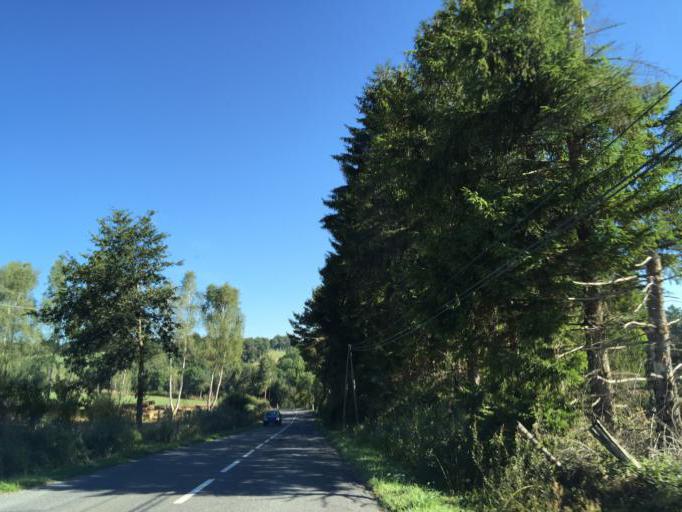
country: FR
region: Midi-Pyrenees
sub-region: Departement de l'Aveyron
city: Pont-de-Salars
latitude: 44.3083
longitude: 2.7360
